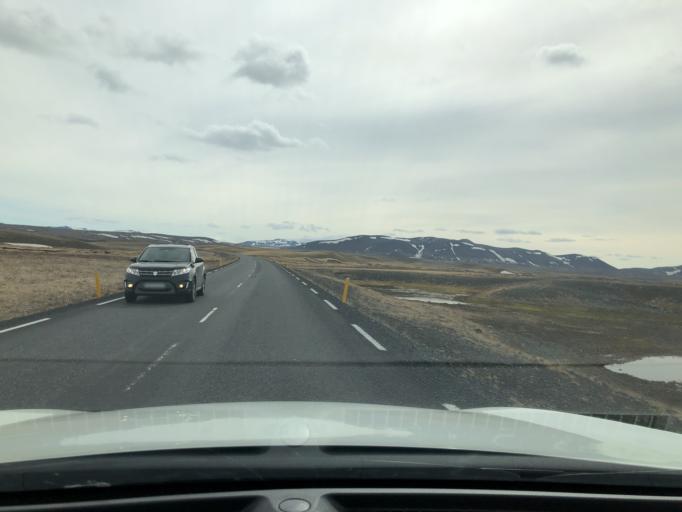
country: IS
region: Northeast
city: Laugar
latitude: 65.5940
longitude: -16.1227
